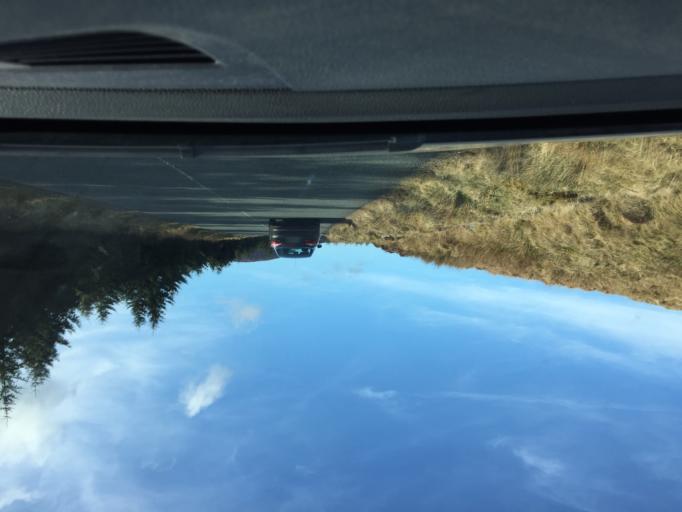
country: IE
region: Leinster
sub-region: Wicklow
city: Valleymount
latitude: 53.0453
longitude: -6.4036
